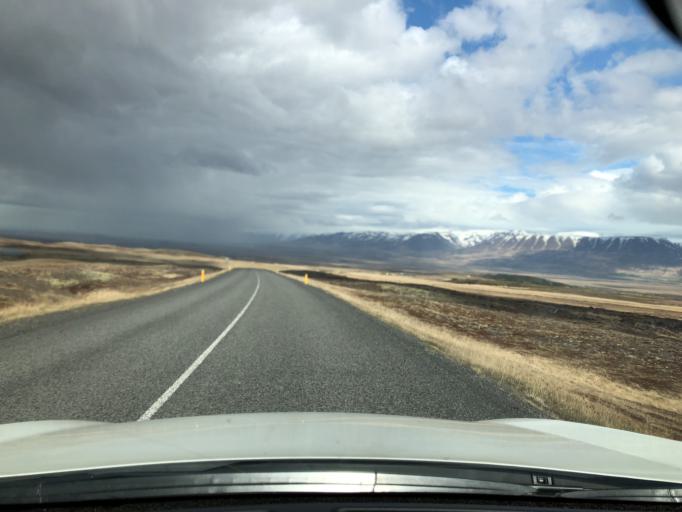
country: IS
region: Northwest
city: Saudarkrokur
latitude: 65.5317
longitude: -19.5136
